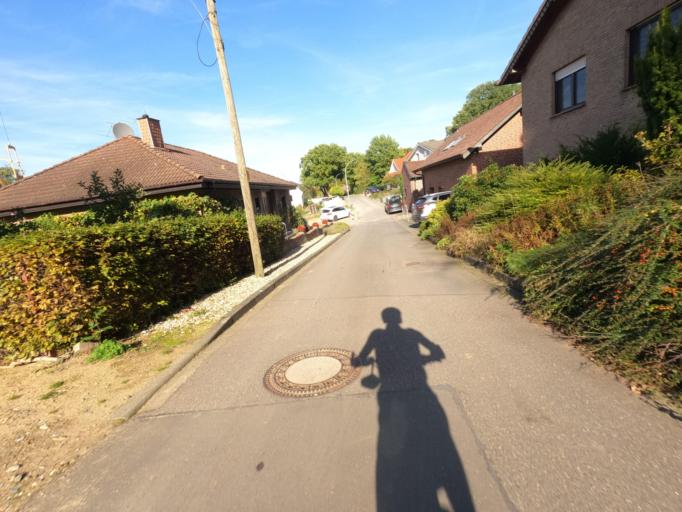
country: DE
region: North Rhine-Westphalia
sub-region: Regierungsbezirk Dusseldorf
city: Niederkruchten
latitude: 51.1776
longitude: 6.2248
